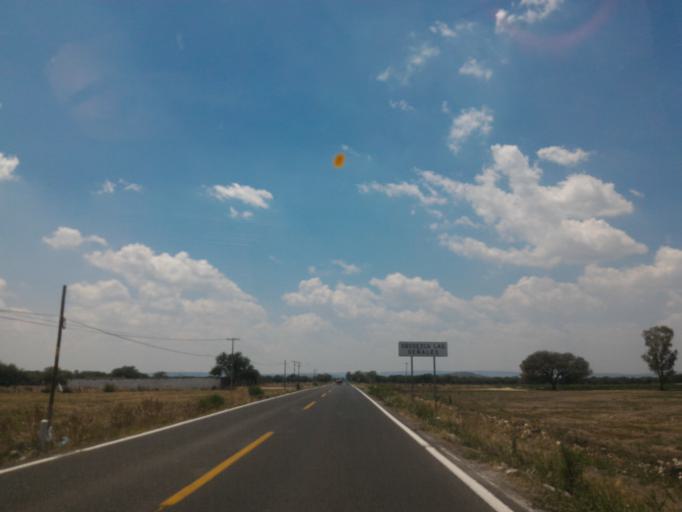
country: MX
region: Guanajuato
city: Ciudad Manuel Doblado
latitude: 20.7641
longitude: -101.9695
